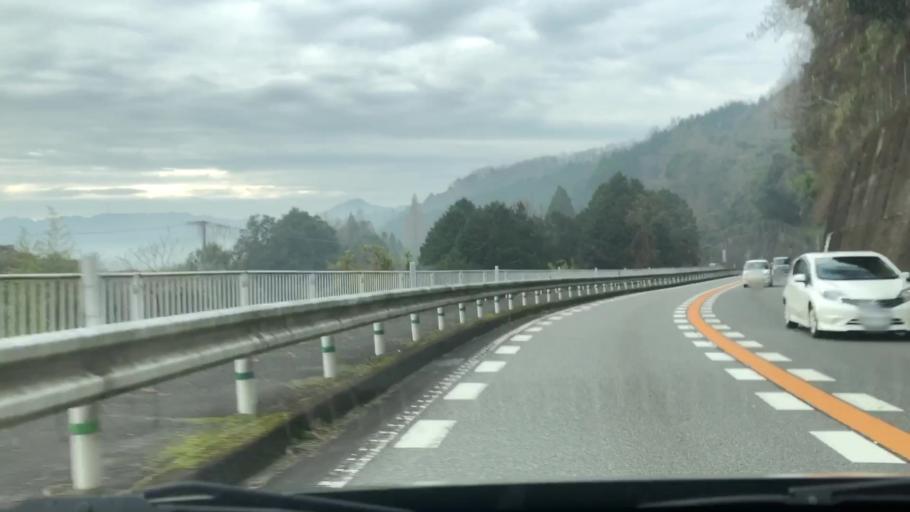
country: JP
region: Oita
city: Usuki
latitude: 33.0261
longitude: 131.6946
